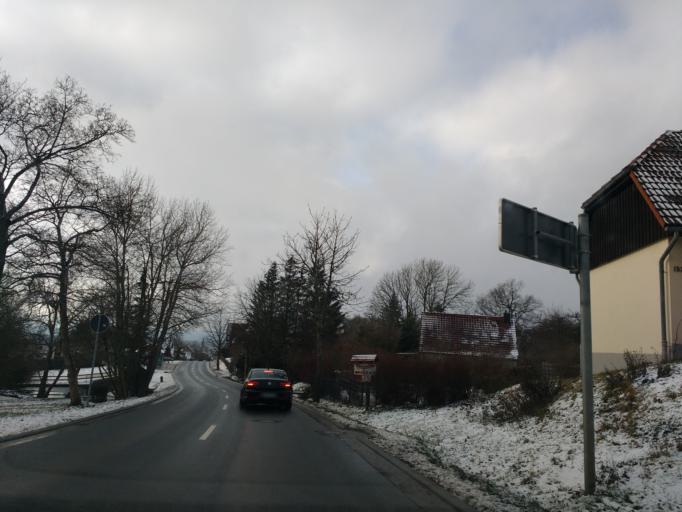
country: DE
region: Saxony-Anhalt
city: Friedrichsbrunn
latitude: 51.6939
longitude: 11.0470
